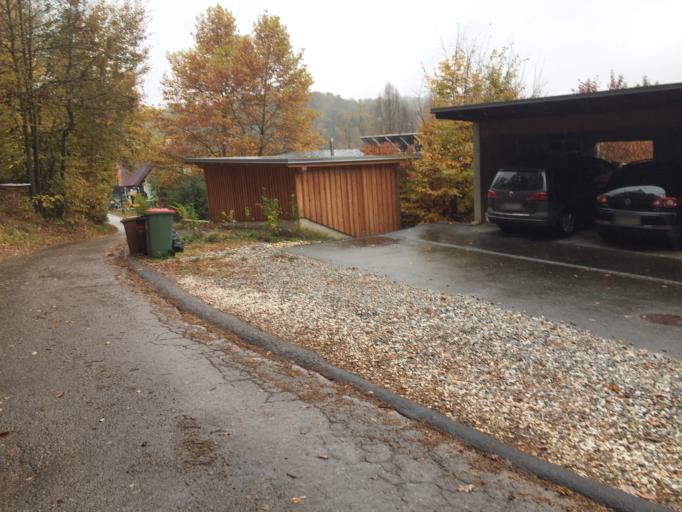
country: AT
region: Styria
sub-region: Politischer Bezirk Graz-Umgebung
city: Hart bei Graz
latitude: 47.0742
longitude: 15.5428
